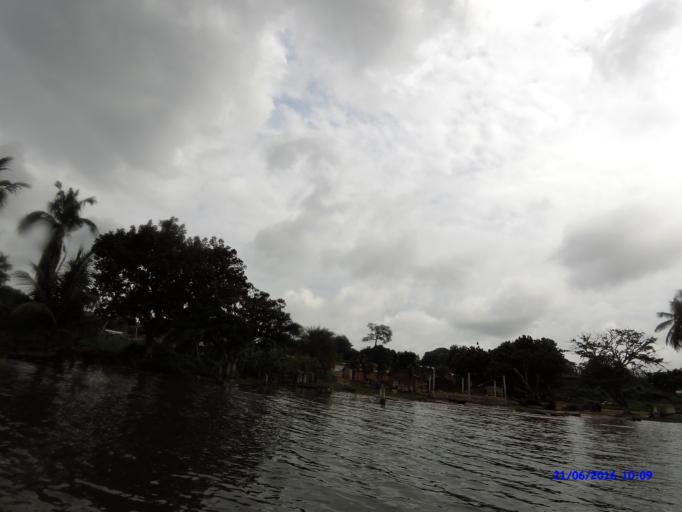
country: BJ
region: Mono
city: Come
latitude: 6.4600
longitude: 1.9274
